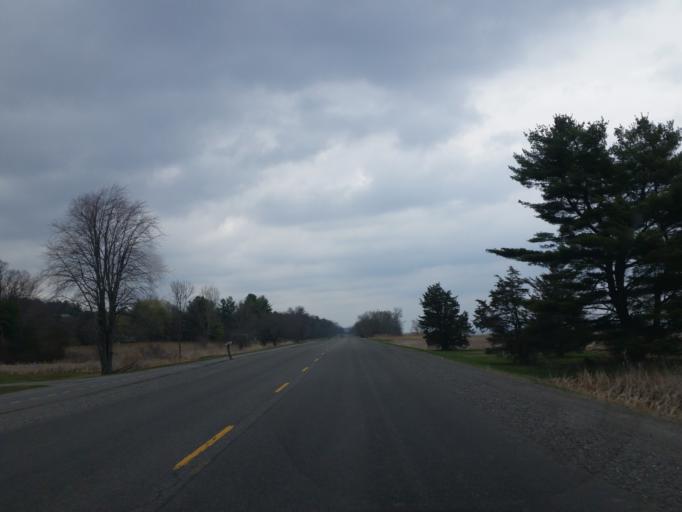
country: US
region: New York
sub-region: Jefferson County
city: Alexandria Bay
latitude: 44.4639
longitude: -75.8476
